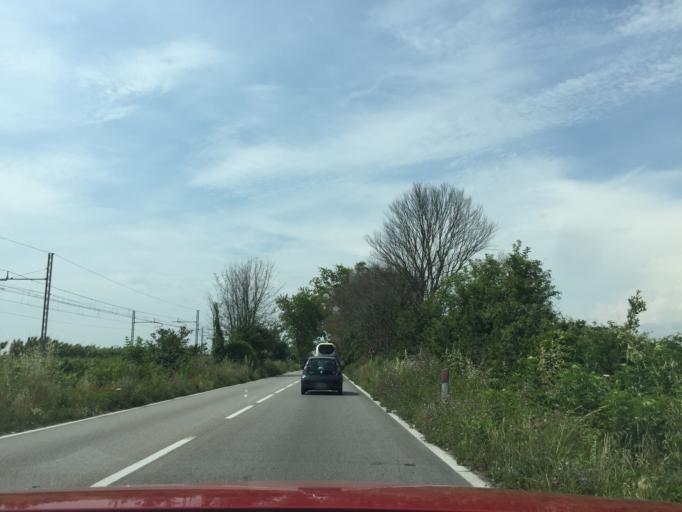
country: IT
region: Tuscany
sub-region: Province of Pisa
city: Migliarino
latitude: 43.7546
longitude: 10.3550
